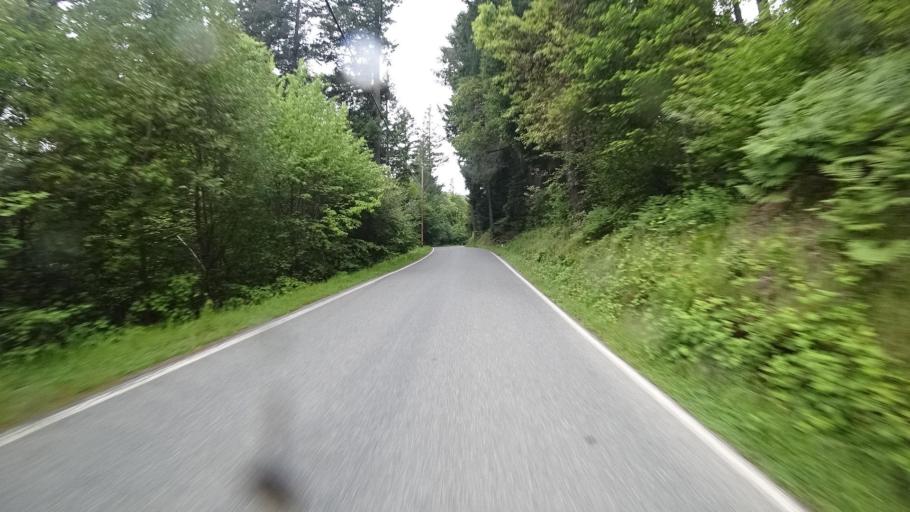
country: US
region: California
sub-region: Humboldt County
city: Willow Creek
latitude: 41.2005
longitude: -123.7480
